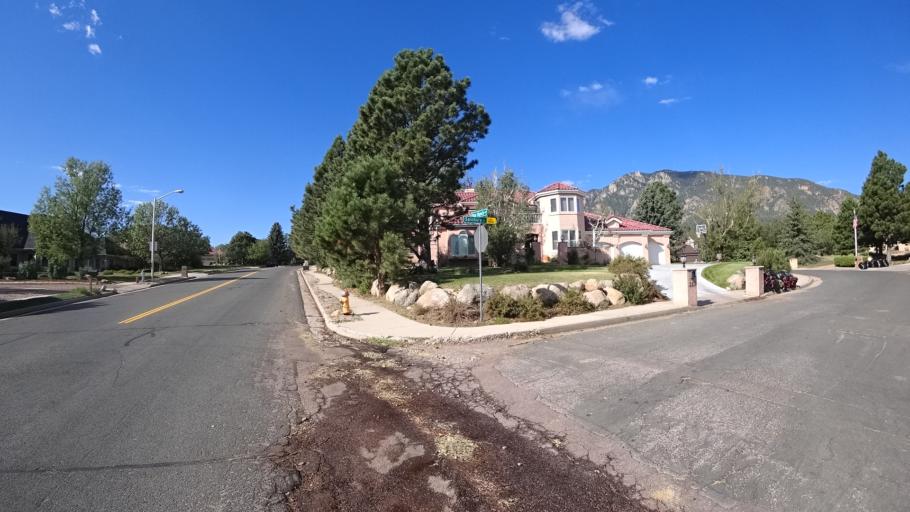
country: US
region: Colorado
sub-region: El Paso County
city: Stratmoor
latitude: 38.7690
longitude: -104.8279
